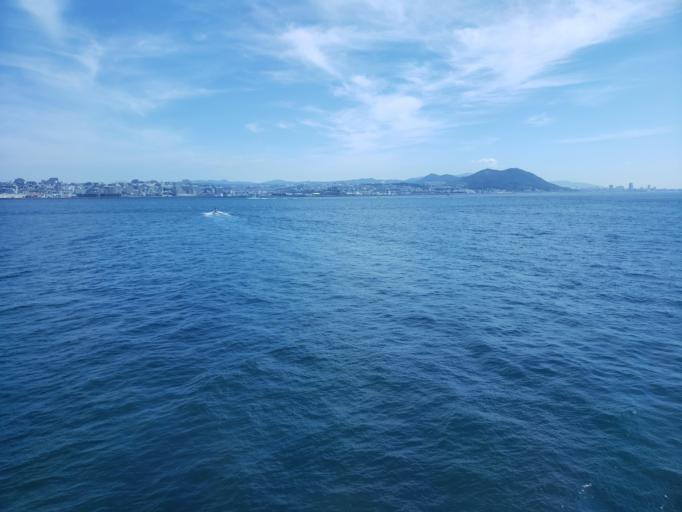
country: JP
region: Hyogo
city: Akashi
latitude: 34.6056
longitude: 135.0482
